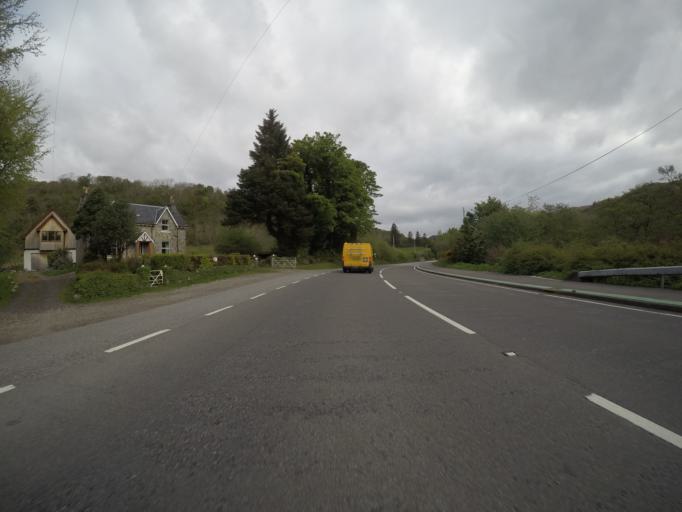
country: GB
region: Scotland
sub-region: Highland
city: Fort William
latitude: 56.7063
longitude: -5.2318
